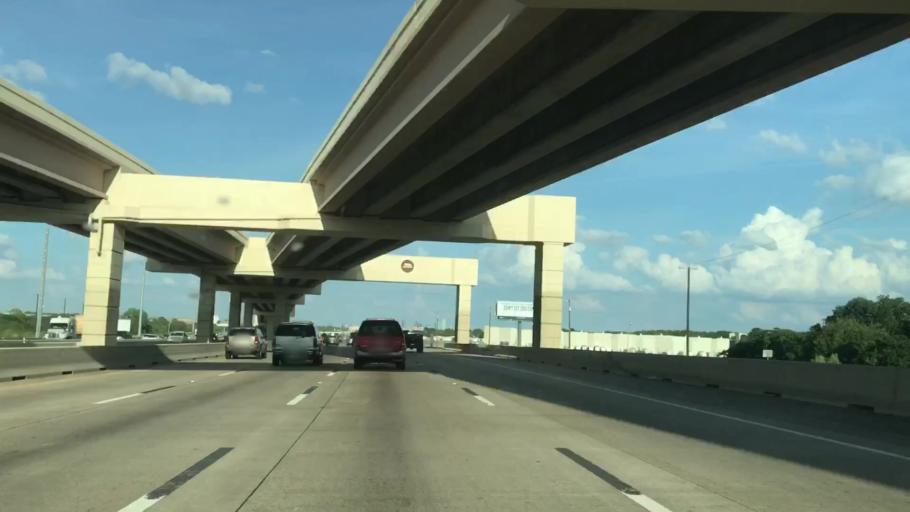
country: US
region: Texas
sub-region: Dallas County
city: Grand Prairie
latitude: 32.7498
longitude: -96.9511
